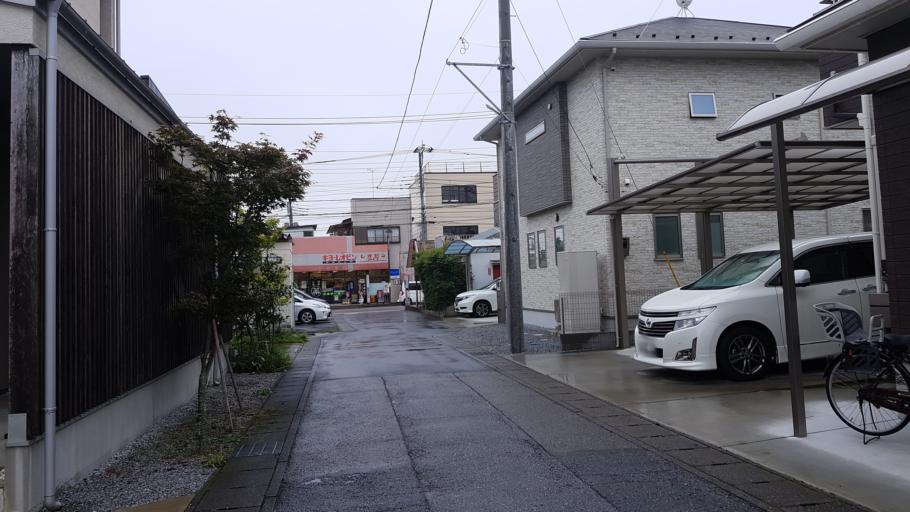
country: JP
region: Tochigi
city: Utsunomiya-shi
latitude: 36.5713
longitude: 139.9188
